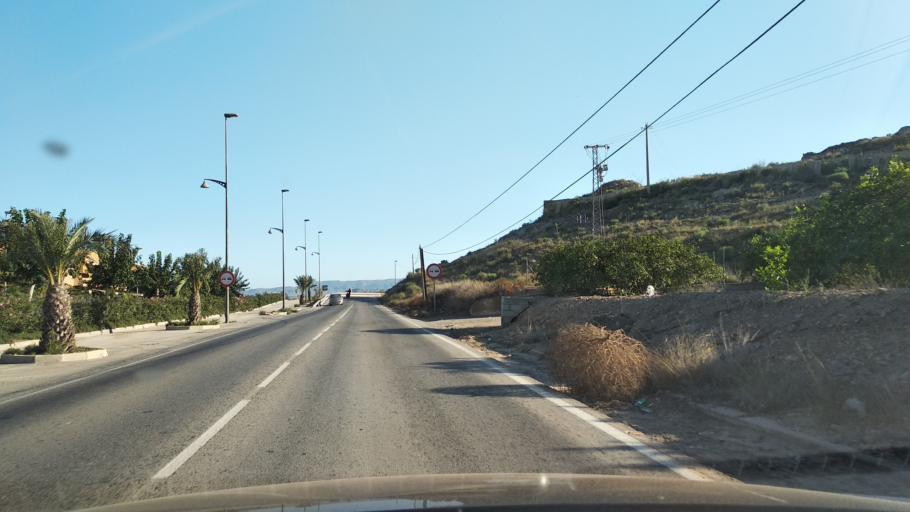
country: ES
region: Murcia
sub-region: Murcia
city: Santomera
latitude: 38.0575
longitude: -1.0530
